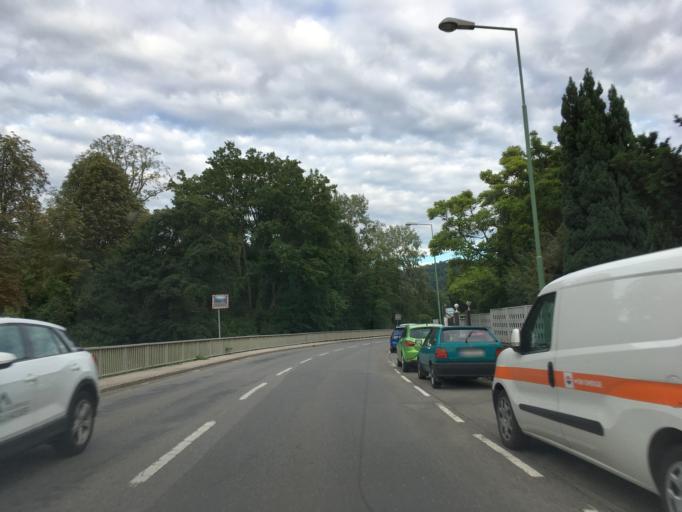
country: AT
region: Lower Austria
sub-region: Politischer Bezirk Wien-Umgebung
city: Klosterneuburg
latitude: 48.3087
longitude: 16.2833
